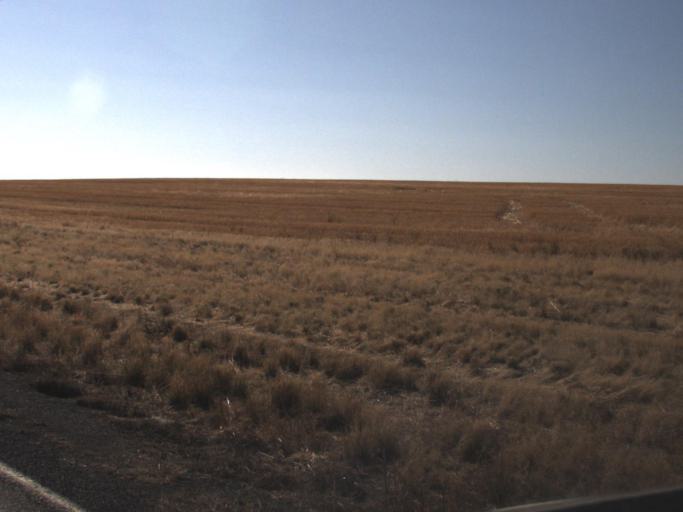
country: US
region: Washington
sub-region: Adams County
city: Ritzville
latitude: 47.0172
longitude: -118.6636
